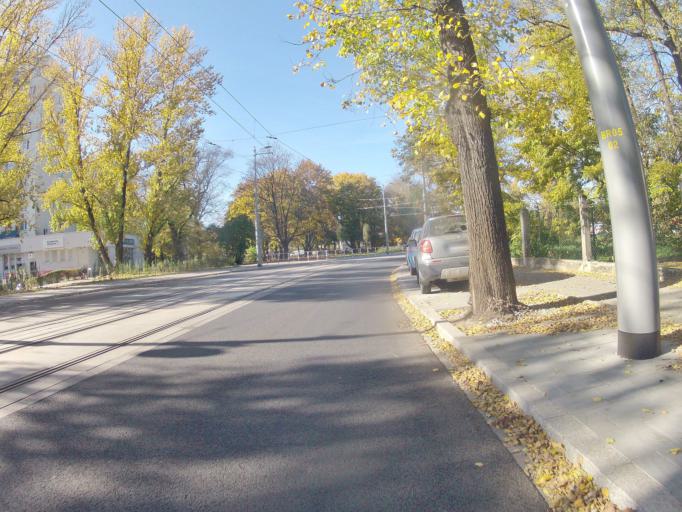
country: PL
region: Lesser Poland Voivodeship
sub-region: Krakow
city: Krakow
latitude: 50.0747
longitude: 19.9083
